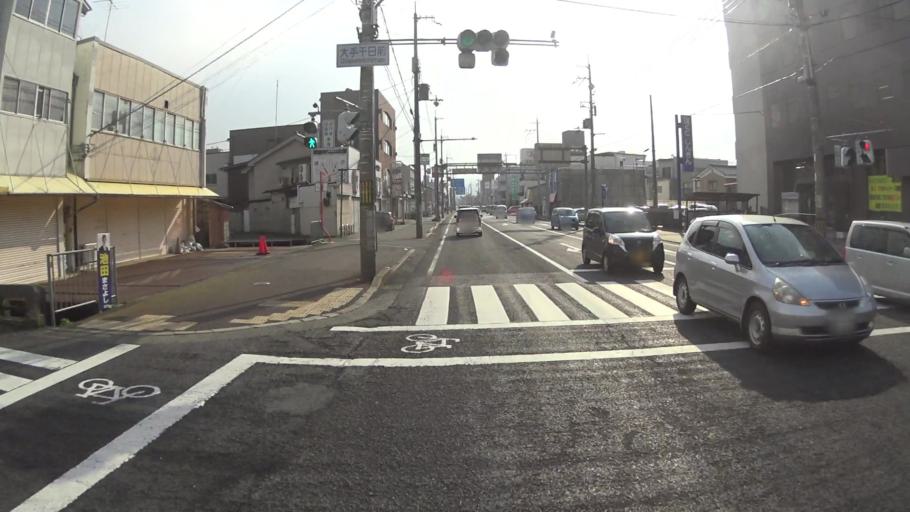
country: JP
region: Kyoto
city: Maizuru
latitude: 35.4453
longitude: 135.3286
